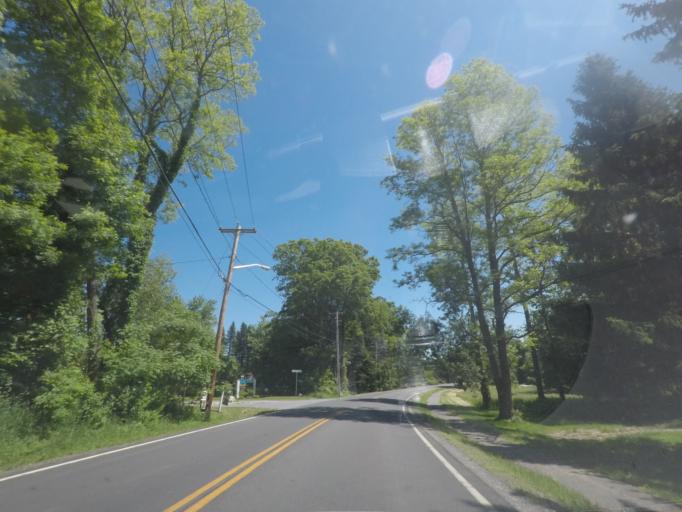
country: US
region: New York
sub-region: Saratoga County
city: Country Knolls
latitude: 42.9033
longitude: -73.8430
